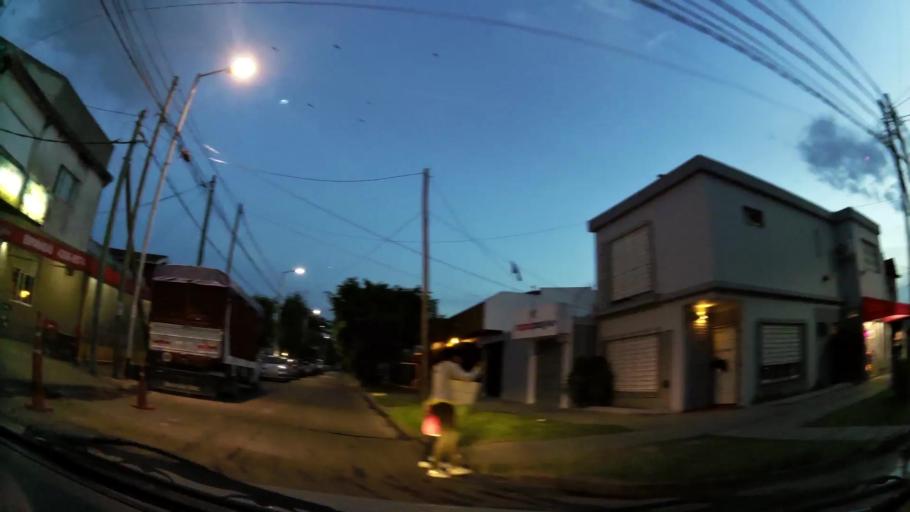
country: AR
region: Buenos Aires
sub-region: Partido de Avellaneda
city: Avellaneda
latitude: -34.6958
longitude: -58.3126
